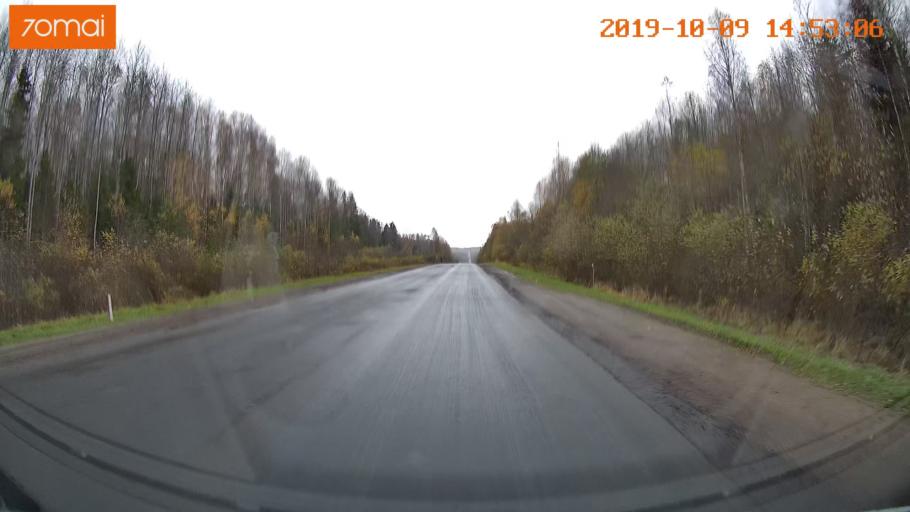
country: RU
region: Kostroma
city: Chistyye Bory
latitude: 58.3719
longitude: 41.6365
